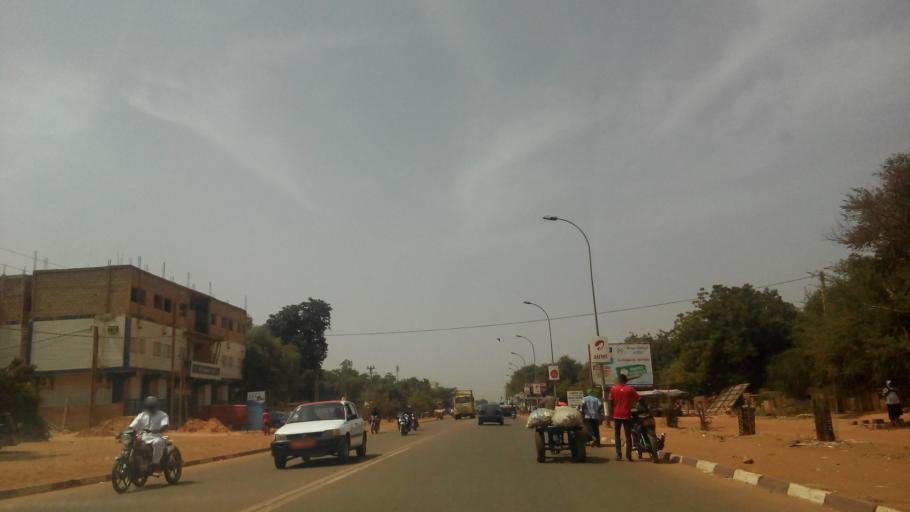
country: NE
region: Niamey
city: Niamey
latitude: 13.5243
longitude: 2.0998
